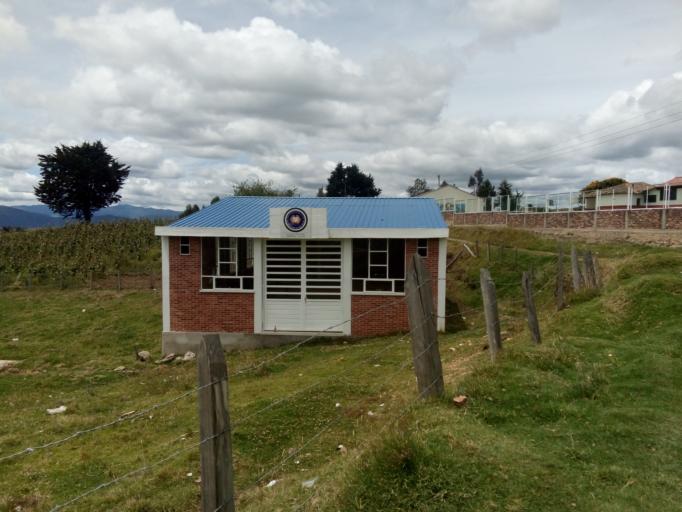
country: CO
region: Boyaca
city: Gameza
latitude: 5.8347
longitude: -72.7951
